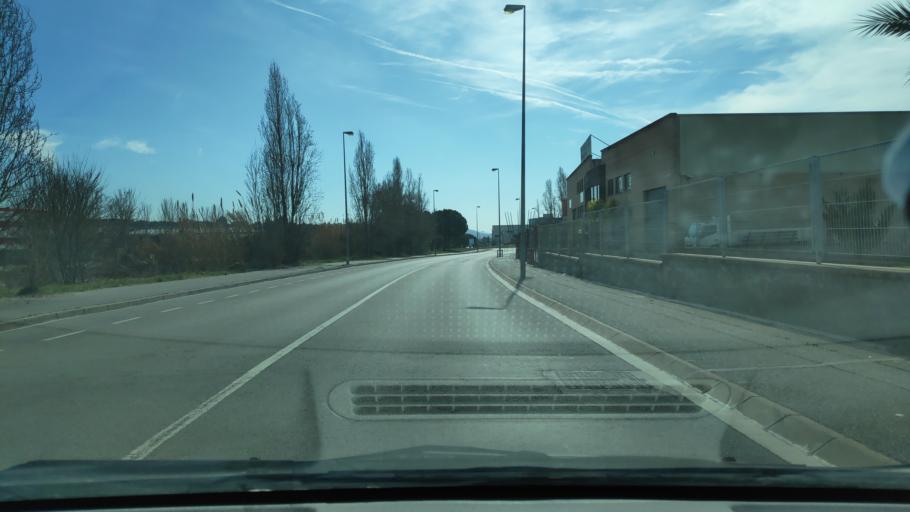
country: ES
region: Catalonia
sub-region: Provincia de Barcelona
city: Rubi
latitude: 41.5095
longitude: 2.0333
